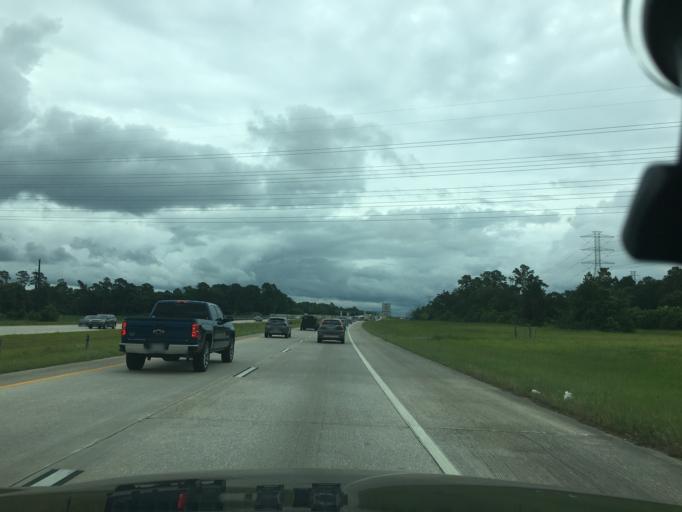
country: US
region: Texas
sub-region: Montgomery County
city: The Woodlands
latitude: 30.0941
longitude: -95.4871
